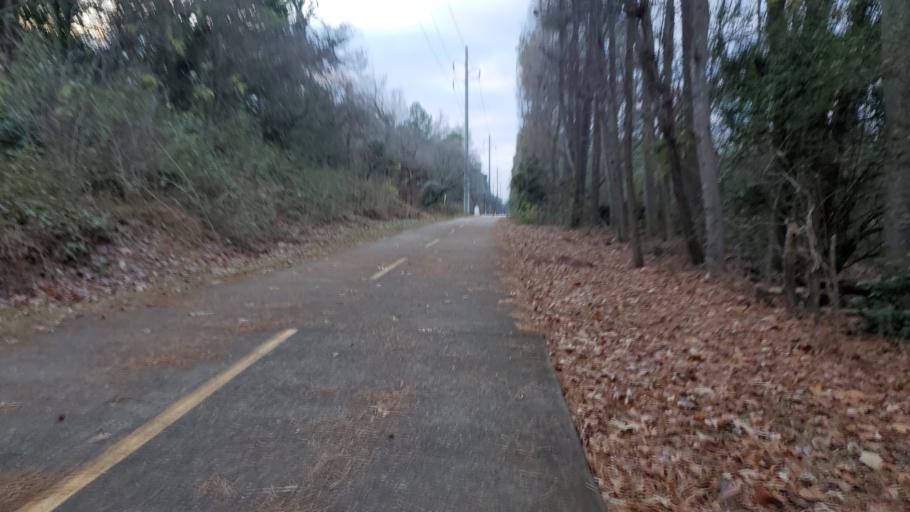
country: US
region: Georgia
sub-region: DeKalb County
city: Clarkston
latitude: 33.8171
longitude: -84.2163
